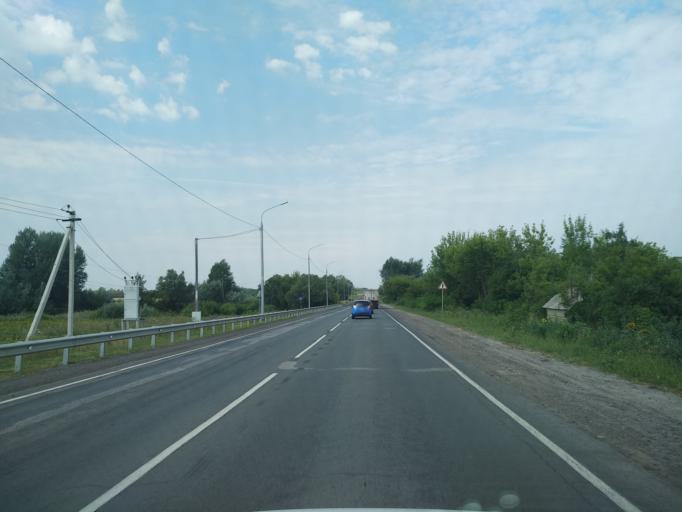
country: RU
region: Voronezj
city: Orlovo
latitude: 51.6797
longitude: 39.6464
